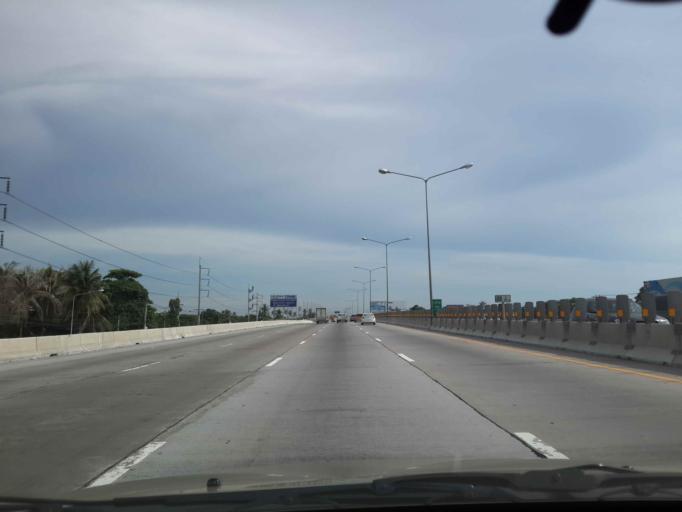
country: TH
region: Chon Buri
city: Si Racha
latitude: 13.1832
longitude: 100.9962
